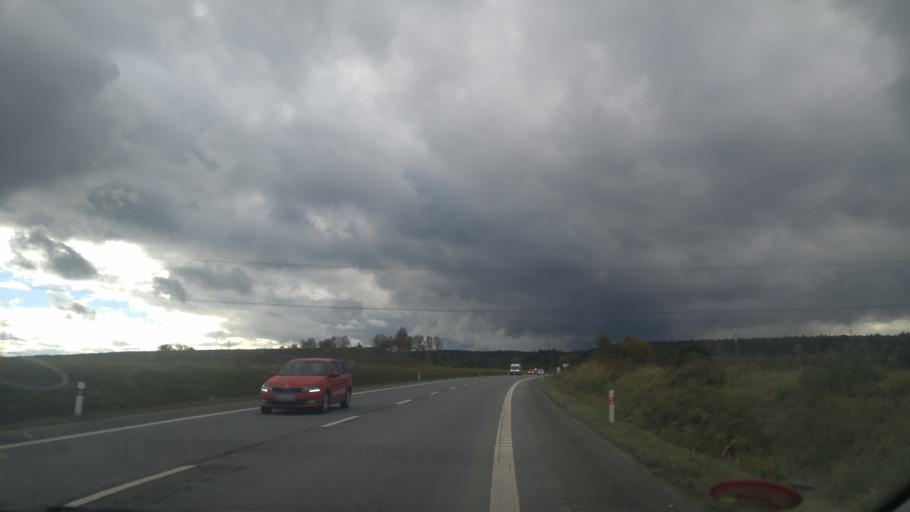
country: CZ
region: Jihocesky
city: Sevetin
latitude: 49.1145
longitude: 14.5833
